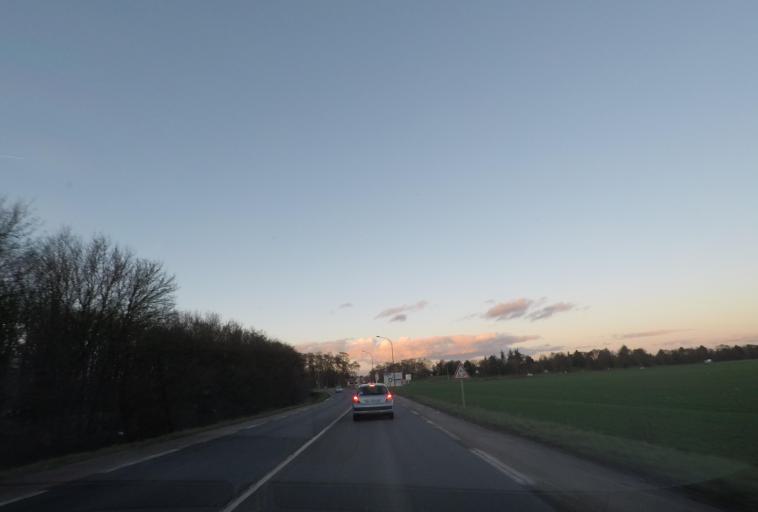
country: FR
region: Ile-de-France
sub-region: Departement de l'Essonne
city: Bondoufle
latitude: 48.6006
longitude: 2.3722
